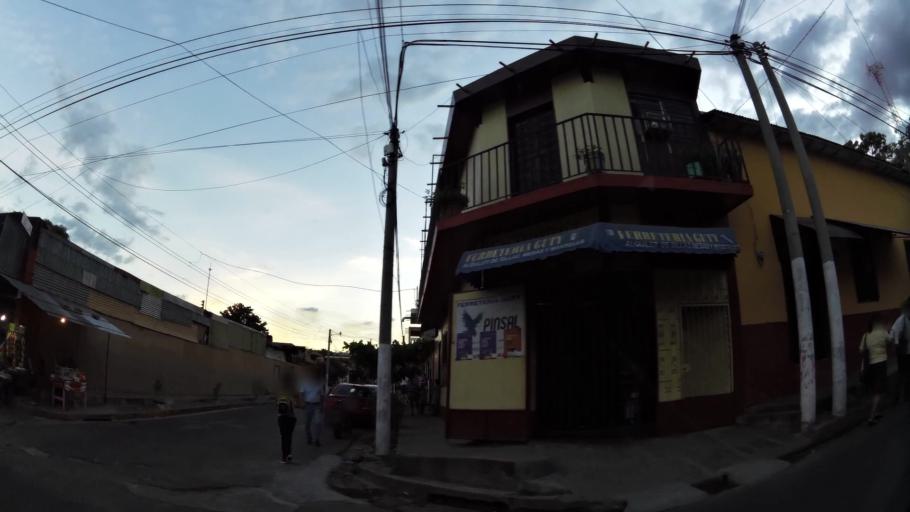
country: SV
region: San Vicente
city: San Vicente
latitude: 13.6413
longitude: -88.7887
